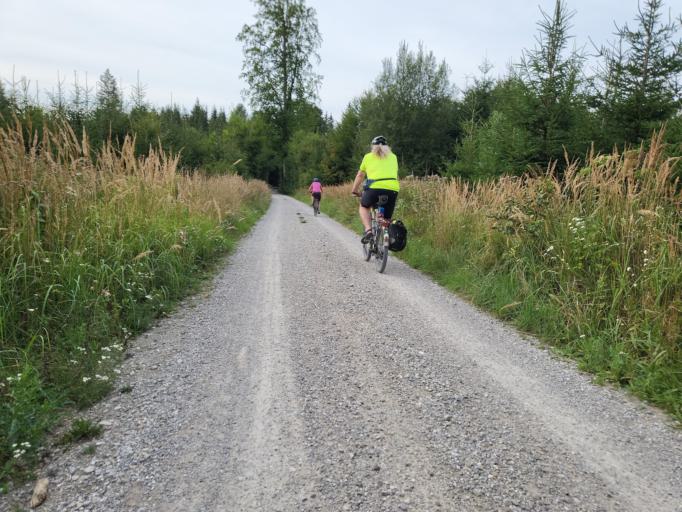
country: DE
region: Bavaria
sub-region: Upper Bavaria
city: Aying
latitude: 47.9870
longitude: 11.7639
